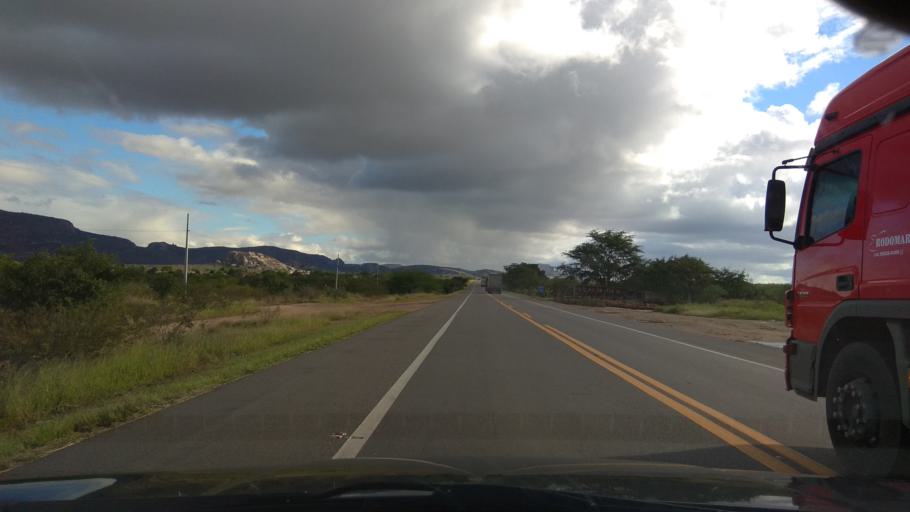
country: BR
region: Bahia
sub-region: Castro Alves
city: Castro Alves
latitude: -12.6985
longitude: -39.7081
